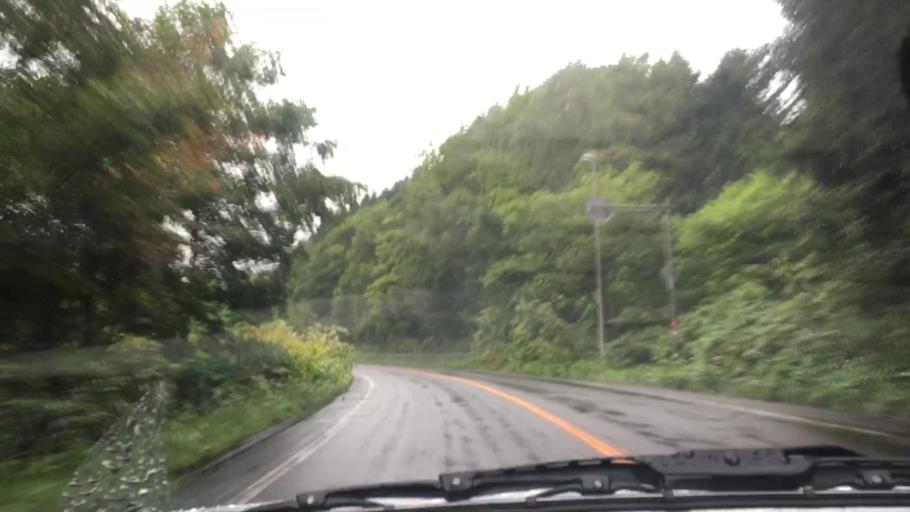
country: JP
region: Hokkaido
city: Niseko Town
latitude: 42.6034
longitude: 140.6164
